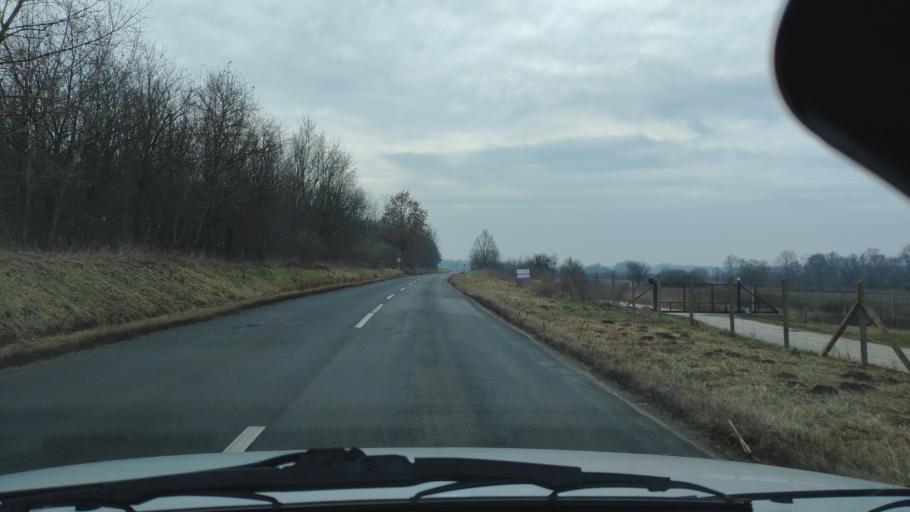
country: HU
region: Zala
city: Nagykanizsa
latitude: 46.5298
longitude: 16.9825
